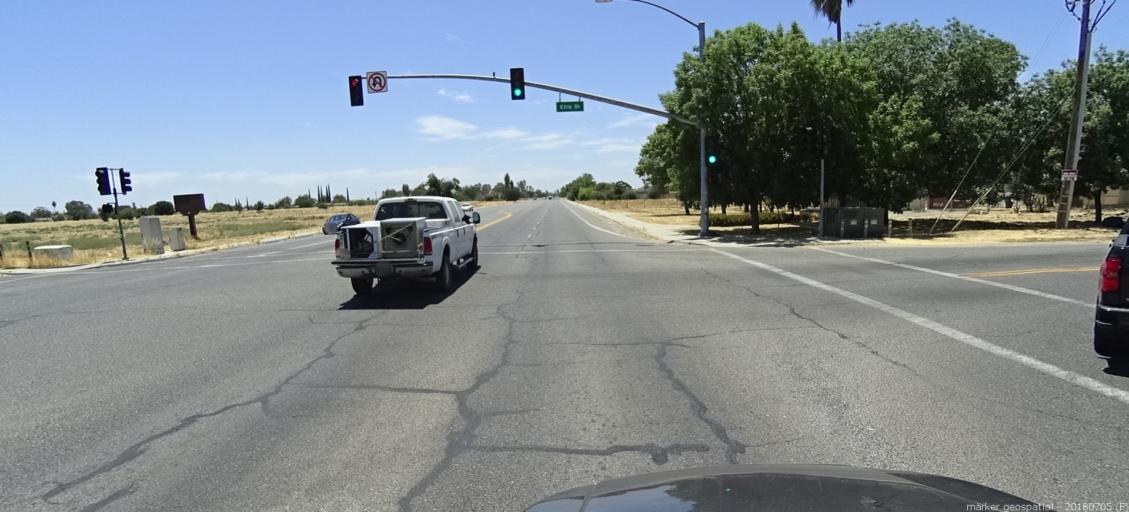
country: US
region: California
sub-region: Madera County
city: Madera
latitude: 36.9870
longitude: -120.0743
